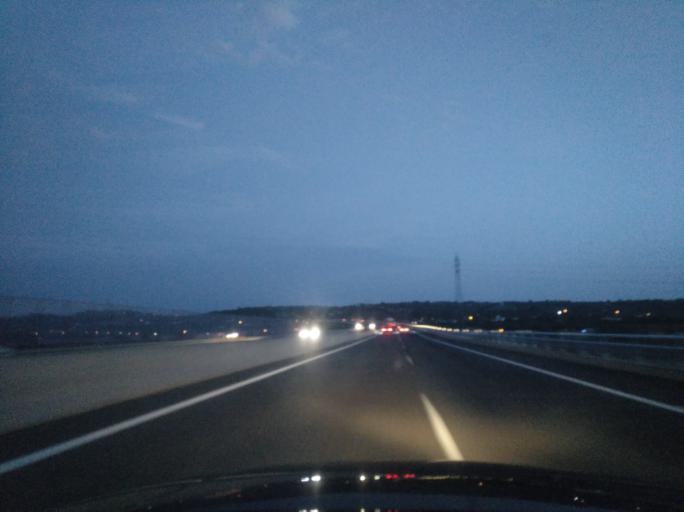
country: PT
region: Faro
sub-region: Lagoa
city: Lagoa
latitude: 37.1448
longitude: -8.4186
